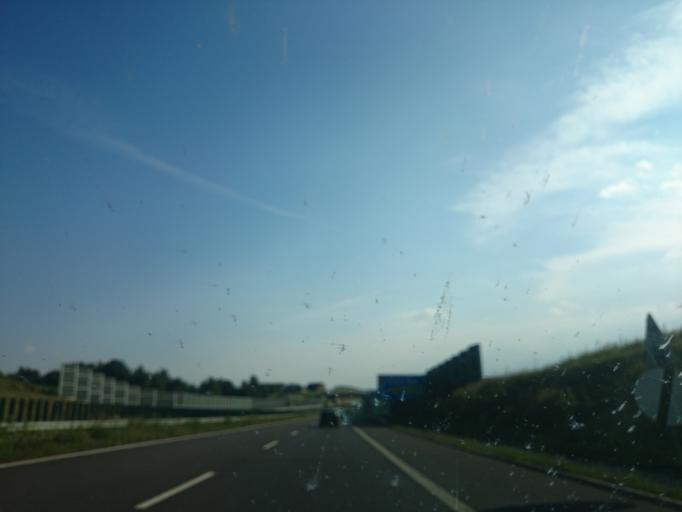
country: PL
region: Silesian Voivodeship
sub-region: Powiat wodzislawski
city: Polomia
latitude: 49.9865
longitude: 18.5635
